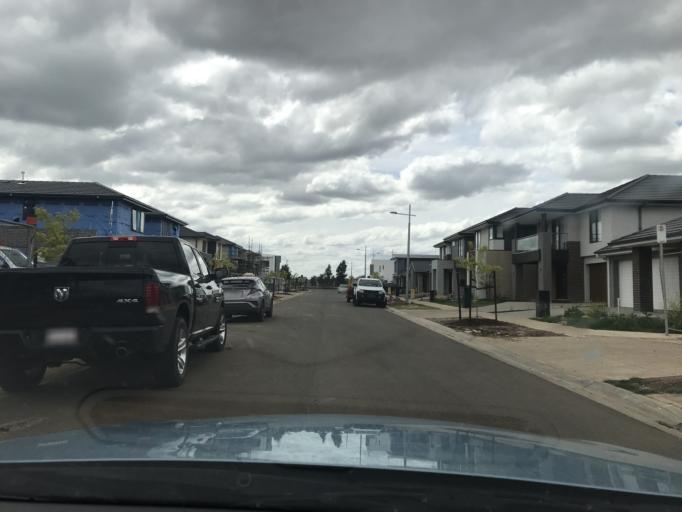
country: AU
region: Victoria
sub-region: Wyndham
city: Williams Landing
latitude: -37.8635
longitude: 144.7518
